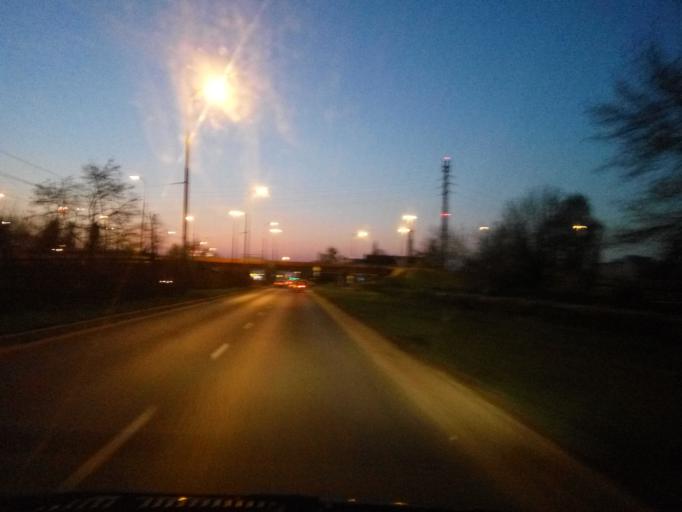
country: PL
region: Lower Silesian Voivodeship
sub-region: Powiat wroclawski
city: Wroclaw
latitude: 51.0861
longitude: 17.0707
